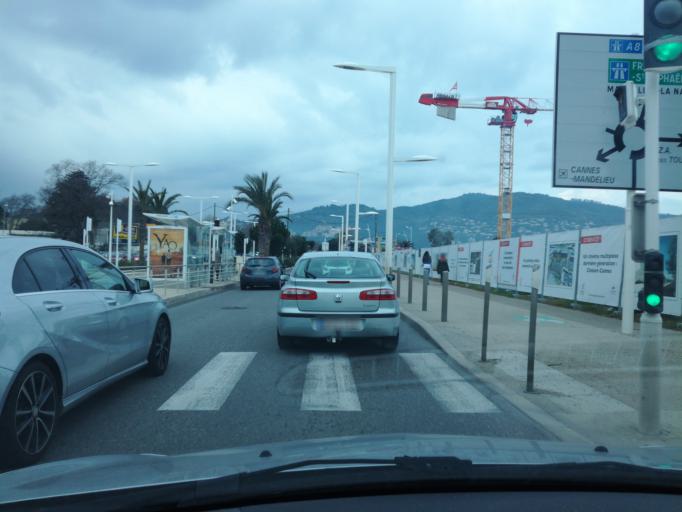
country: FR
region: Provence-Alpes-Cote d'Azur
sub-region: Departement des Alpes-Maritimes
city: Mandelieu-la-Napoule
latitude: 43.5504
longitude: 6.9593
